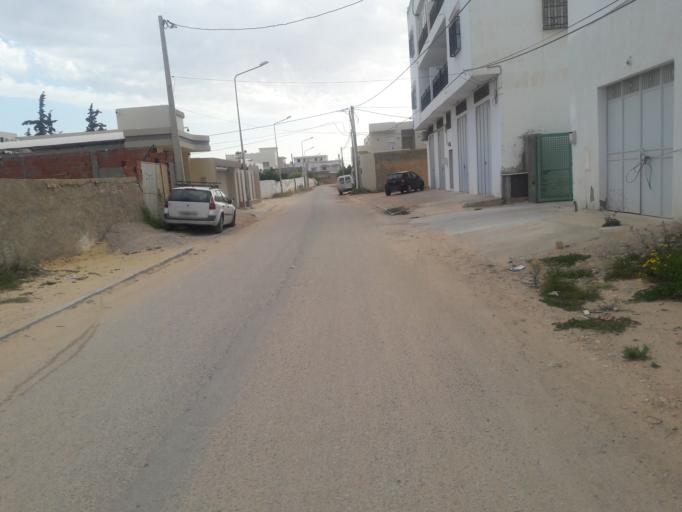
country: TN
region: Safaqis
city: Al Qarmadah
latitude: 34.8139
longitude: 10.7460
